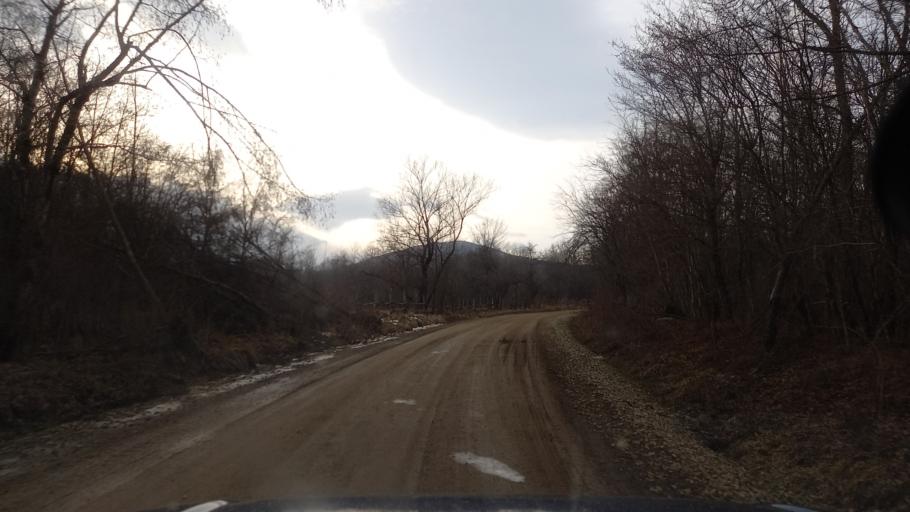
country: RU
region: Adygeya
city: Kamennomostskiy
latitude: 44.1384
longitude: 40.2644
